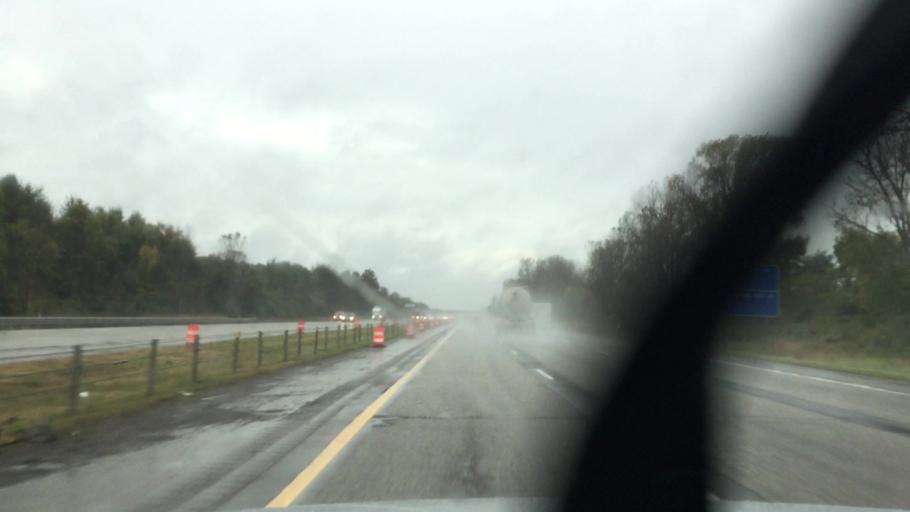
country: US
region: Michigan
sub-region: Berrien County
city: Benton Heights
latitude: 42.1081
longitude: -86.3983
